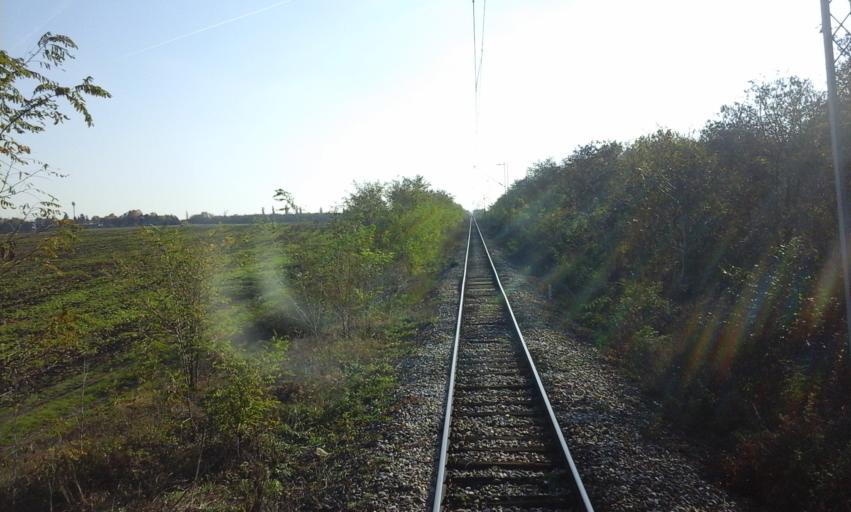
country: RS
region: Autonomna Pokrajina Vojvodina
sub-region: Severnobacki Okrug
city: Backa Topola
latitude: 45.7851
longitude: 19.6477
